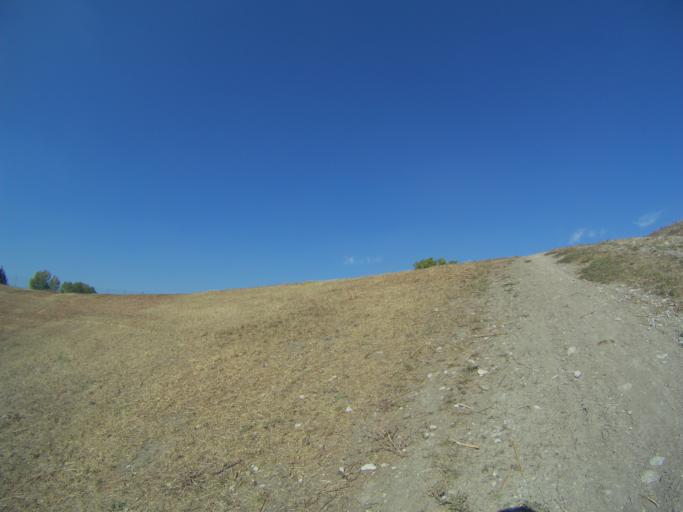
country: IT
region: Emilia-Romagna
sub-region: Provincia di Reggio Emilia
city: Forche
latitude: 44.6435
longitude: 10.5869
